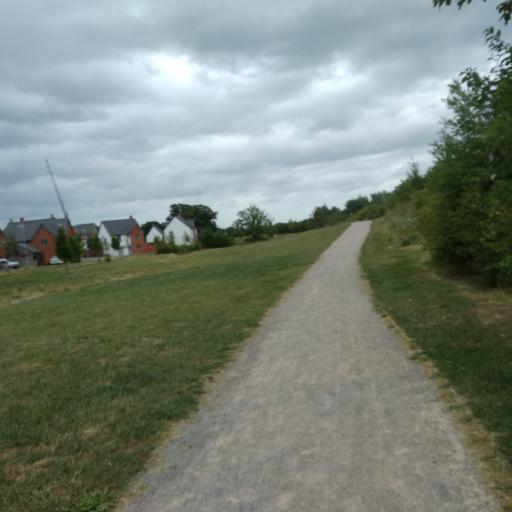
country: GB
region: England
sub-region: Kent
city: Ashford
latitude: 51.1582
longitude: 0.8488
